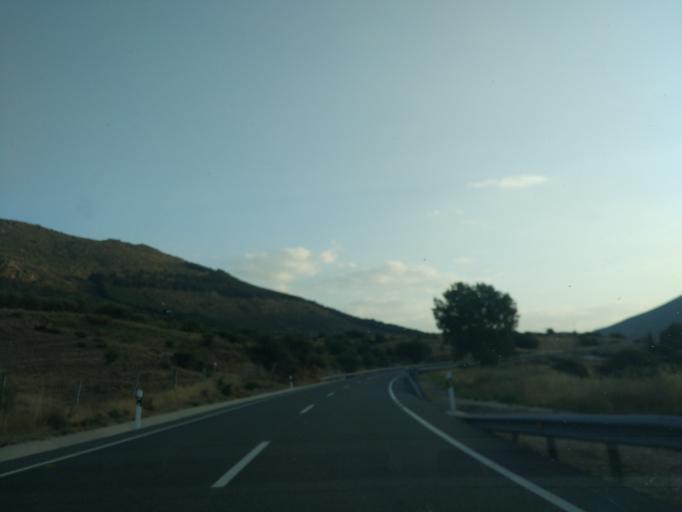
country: ES
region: Castille and Leon
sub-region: Provincia de Avila
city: Mengamunoz
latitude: 40.5035
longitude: -4.9940
